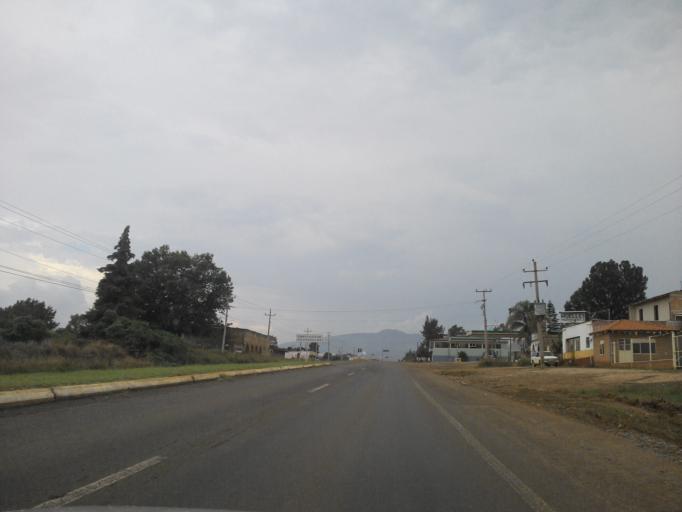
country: MX
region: Jalisco
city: San Jose de Gracia
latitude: 20.7387
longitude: -102.5143
